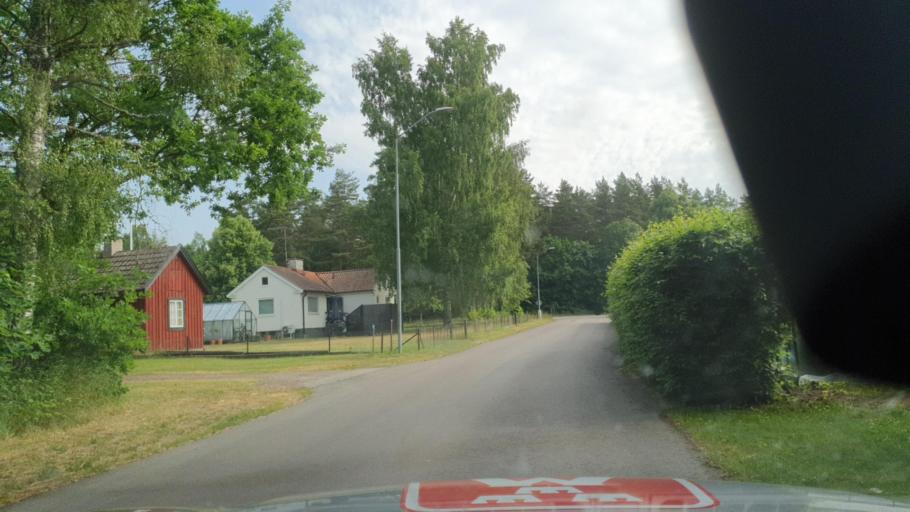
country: SE
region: Kalmar
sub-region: Kalmar Kommun
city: Ljungbyholm
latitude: 56.5912
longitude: 16.1495
